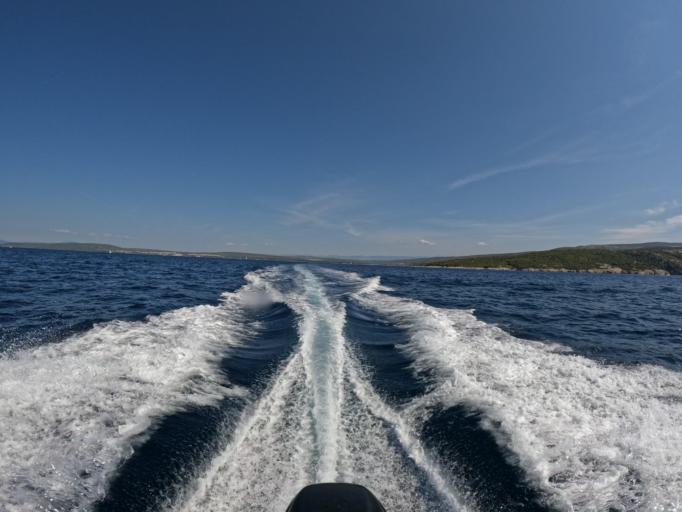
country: HR
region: Primorsko-Goranska
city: Punat
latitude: 44.9715
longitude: 14.6088
